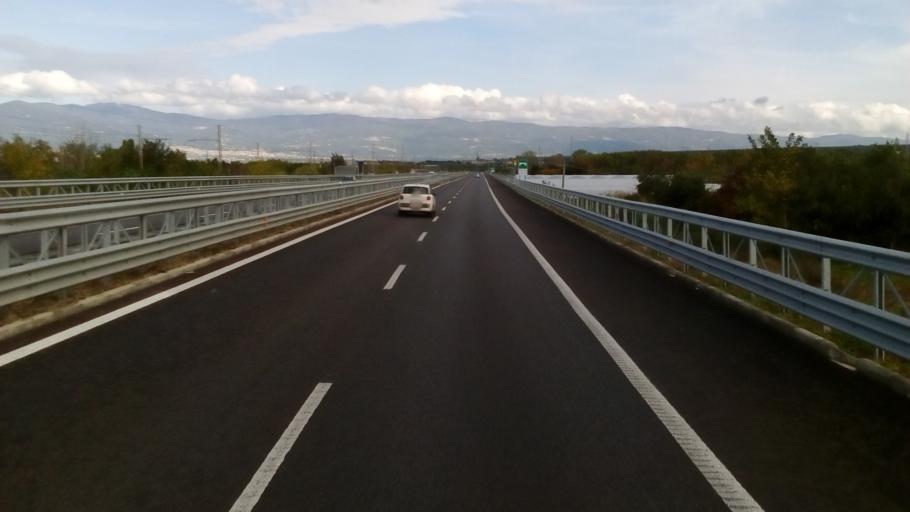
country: IT
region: Calabria
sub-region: Provincia di Catanzaro
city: Acconia
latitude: 38.8464
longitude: 16.2657
